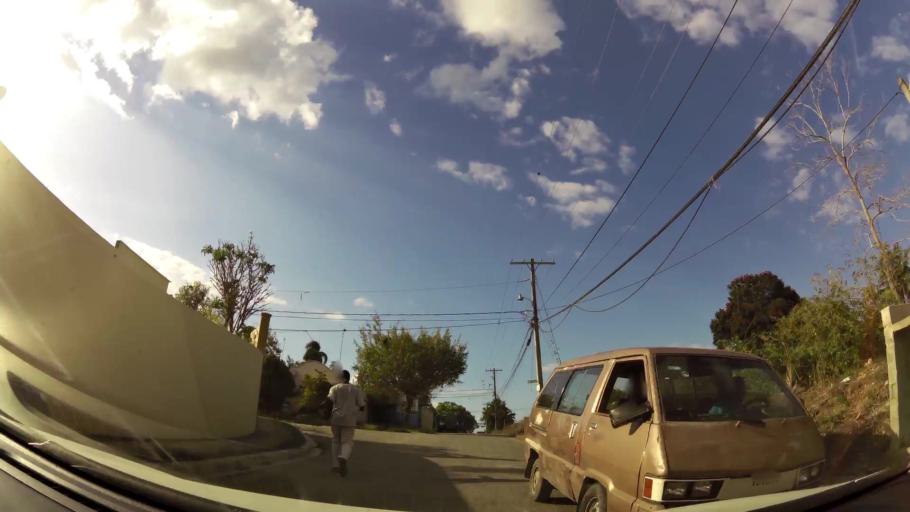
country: DO
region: Nacional
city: Ensanche Luperon
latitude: 18.5557
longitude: -69.8949
